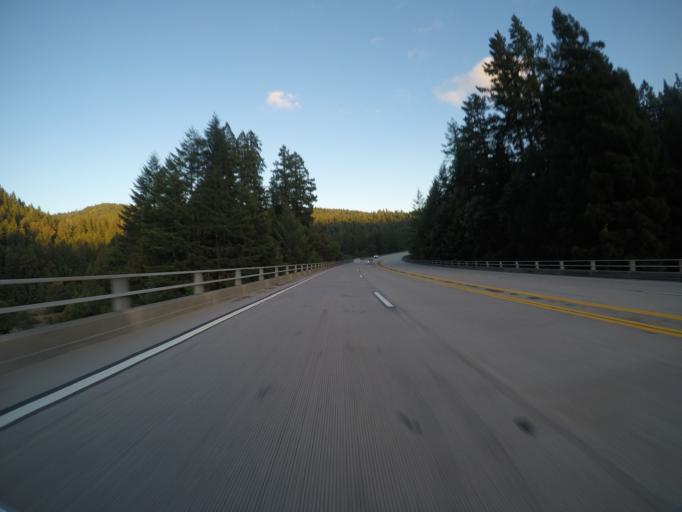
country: US
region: California
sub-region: Humboldt County
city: Redway
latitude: 39.9580
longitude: -123.7812
